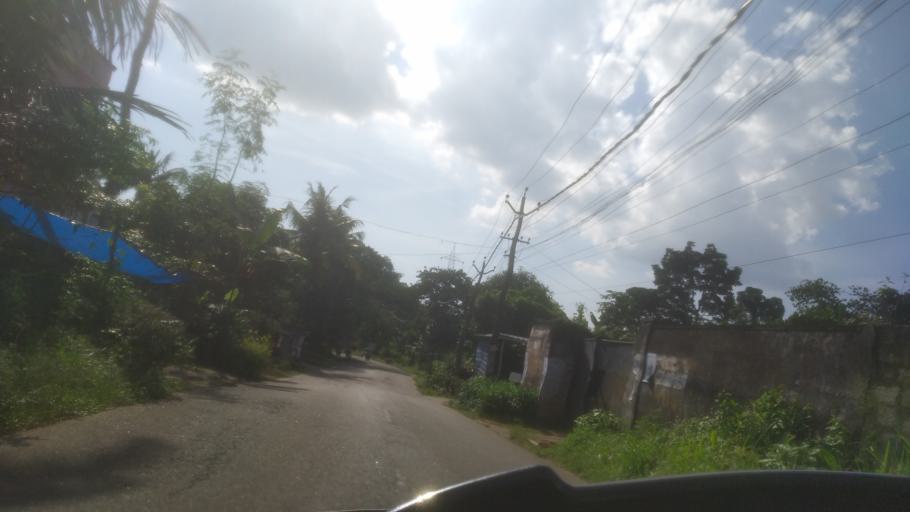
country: IN
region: Kerala
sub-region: Ernakulam
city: Muvattupula
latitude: 9.9982
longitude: 76.6201
